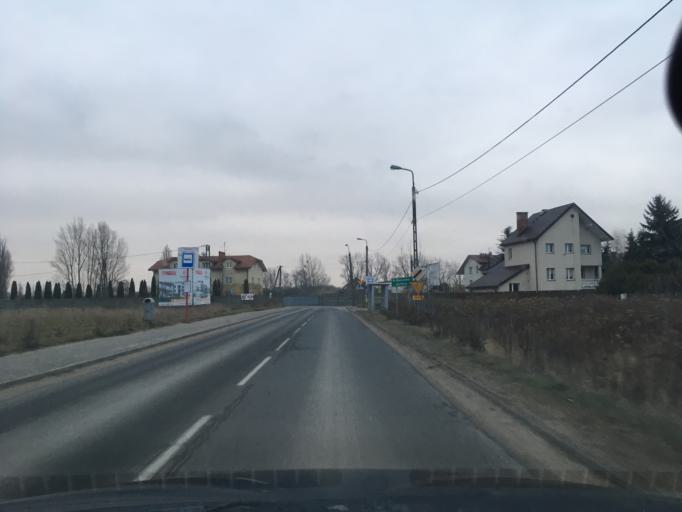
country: PL
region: Masovian Voivodeship
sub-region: Powiat piaseczynski
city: Mysiadlo
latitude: 52.1115
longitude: 20.9838
